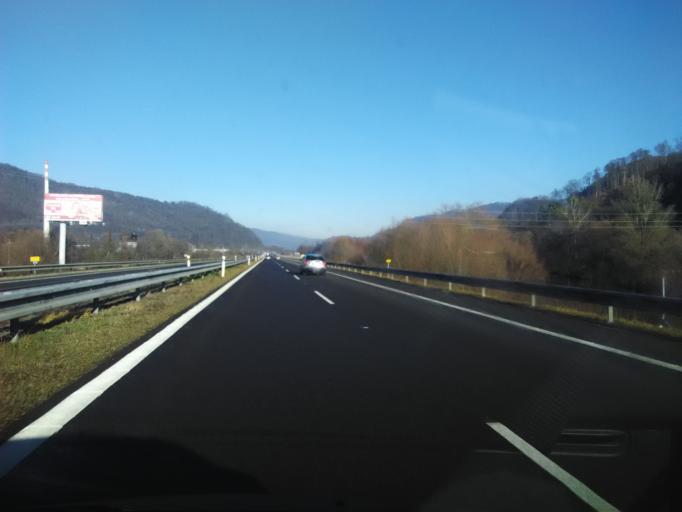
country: SK
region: Banskobystricky
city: Zarnovica
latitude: 48.4839
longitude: 18.7301
